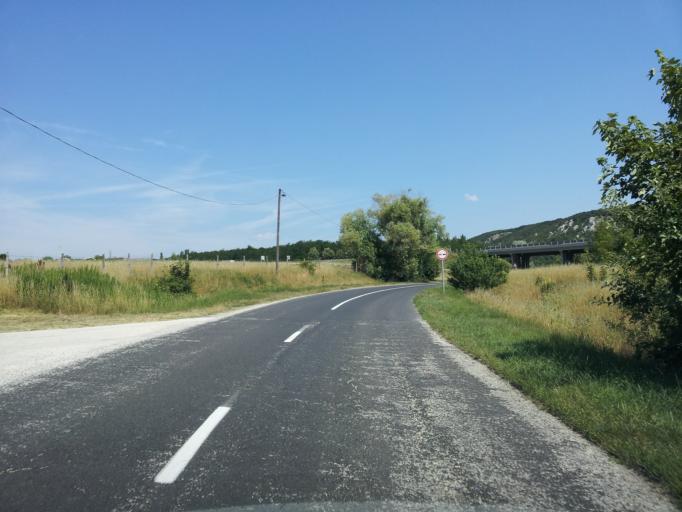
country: HU
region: Fejer
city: Szarliget
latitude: 47.4945
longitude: 18.5647
